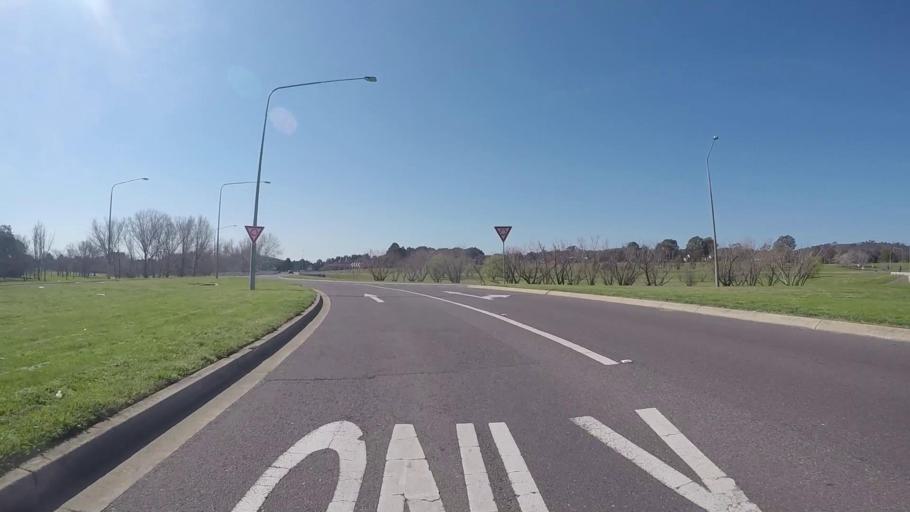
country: AU
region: Australian Capital Territory
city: Forrest
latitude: -35.3365
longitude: 149.0853
